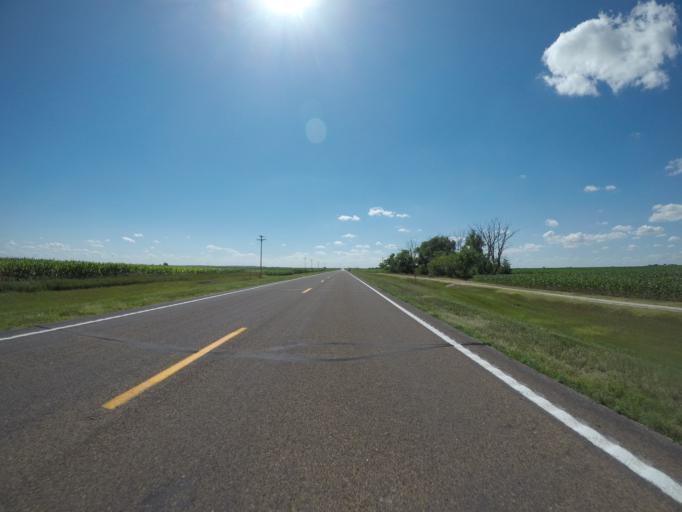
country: US
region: Nebraska
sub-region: Chase County
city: Imperial
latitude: 40.5376
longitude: -101.9360
